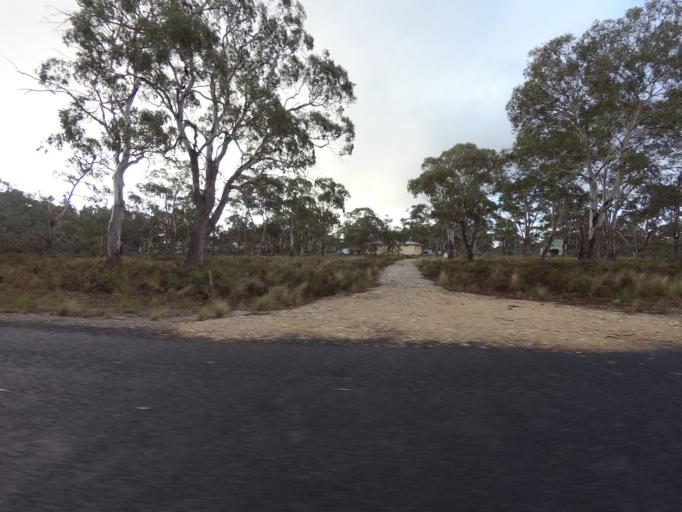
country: AU
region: Tasmania
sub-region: Break O'Day
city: St Helens
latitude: -42.1077
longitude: 148.0726
